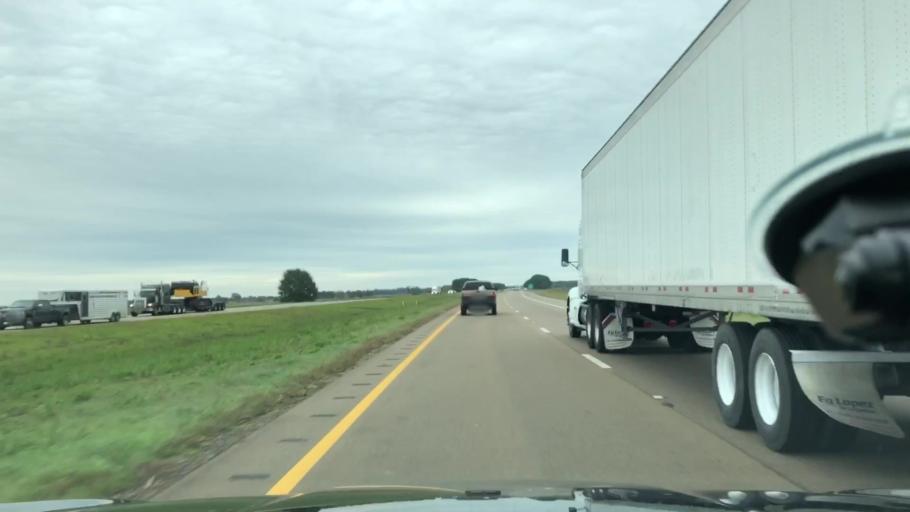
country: US
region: Texas
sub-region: Morris County
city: Omaha
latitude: 33.2901
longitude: -94.7753
